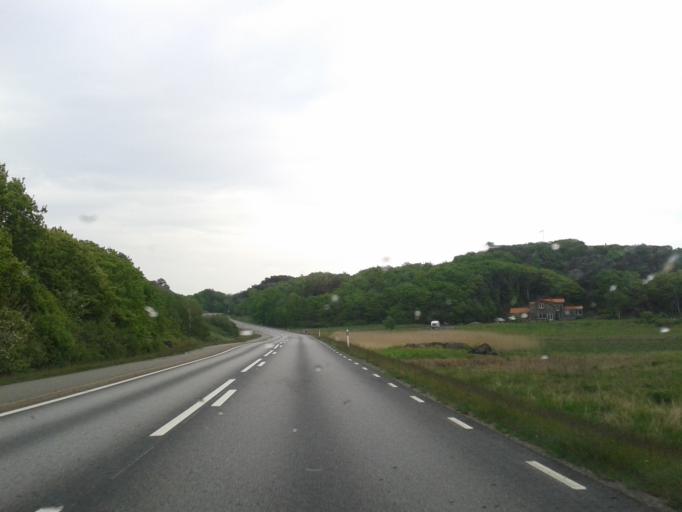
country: SE
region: Vaestra Goetaland
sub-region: Kungalvs Kommun
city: Marstrand
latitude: 57.8936
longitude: 11.6364
